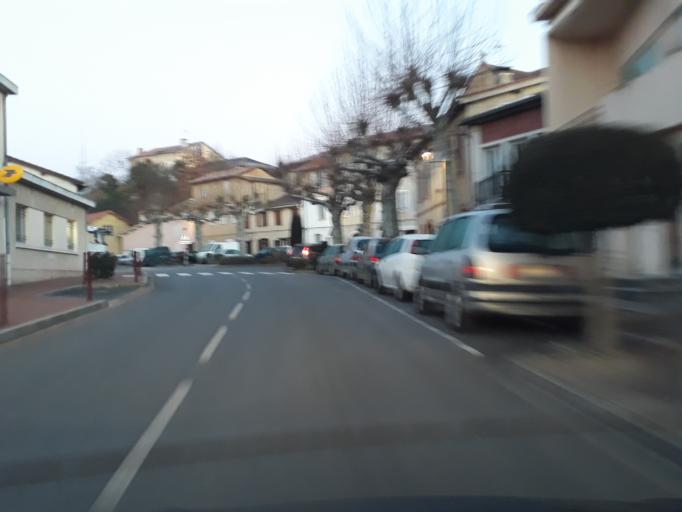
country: FR
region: Midi-Pyrenees
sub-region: Departement du Gers
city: Samatan
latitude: 43.4915
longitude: 0.9297
